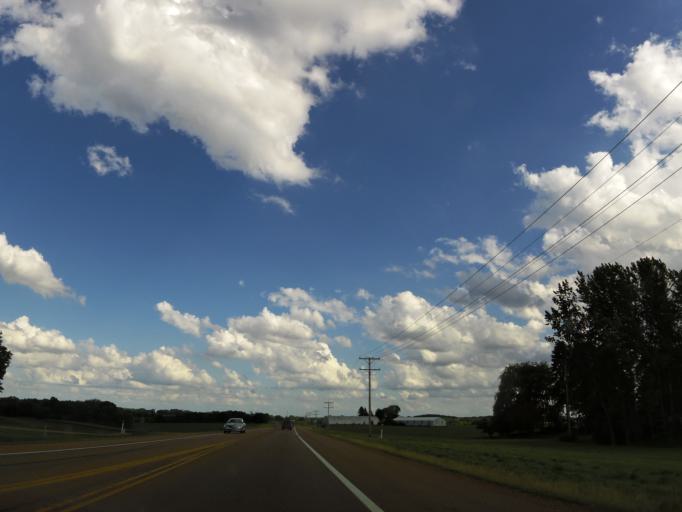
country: US
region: Minnesota
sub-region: Carver County
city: Waconia
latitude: 44.8261
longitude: -93.7443
